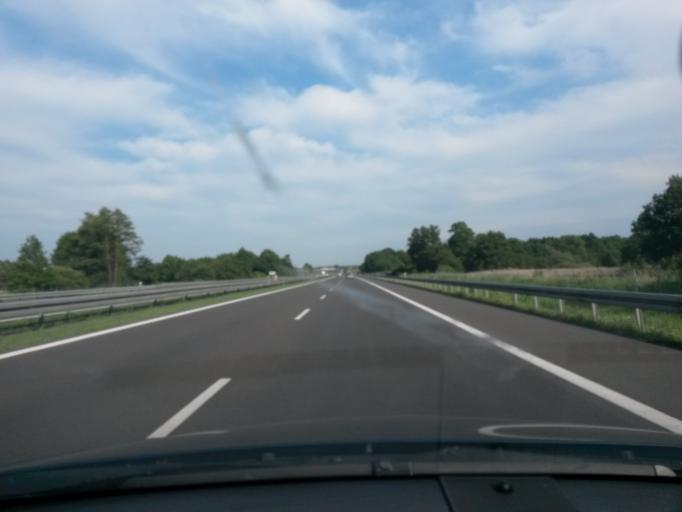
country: PL
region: Greater Poland Voivodeship
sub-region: Powiat koninski
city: Rzgow Pierwszy
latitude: 52.1855
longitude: 18.0914
